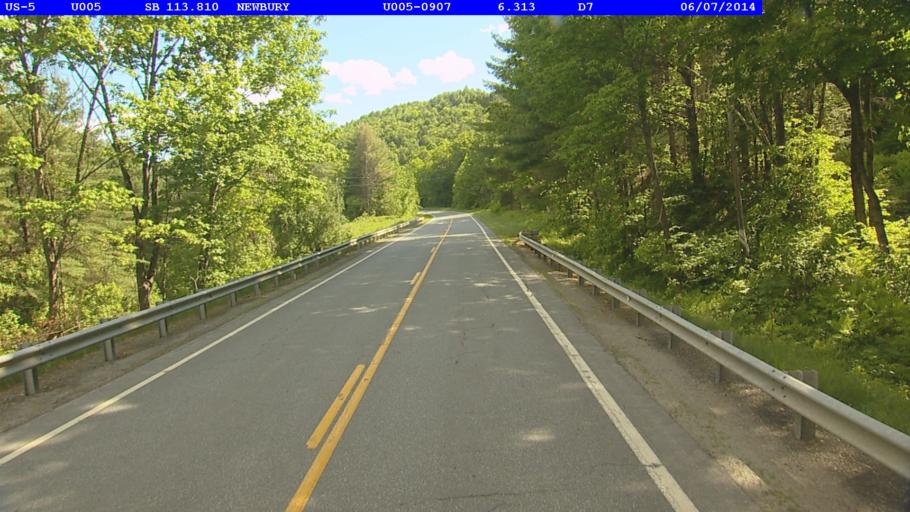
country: US
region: New Hampshire
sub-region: Grafton County
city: North Haverhill
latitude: 44.1112
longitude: -72.0563
